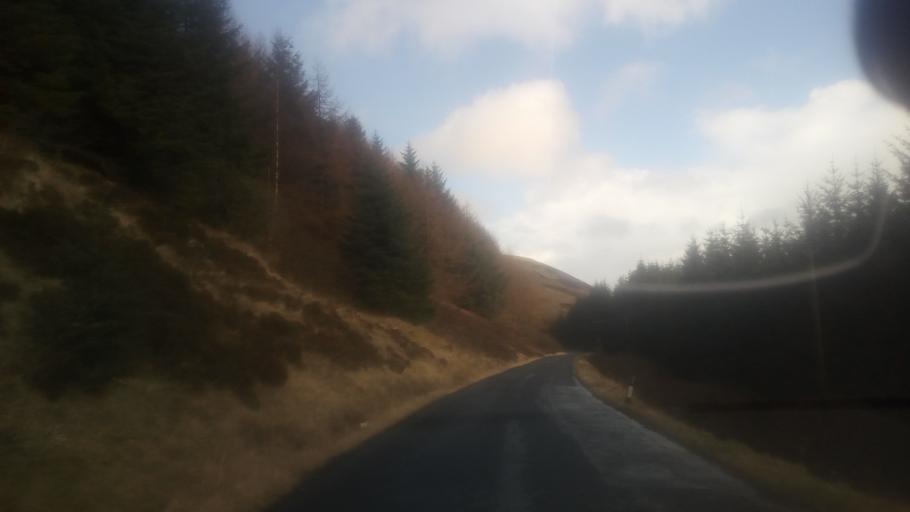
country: GB
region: Scotland
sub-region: The Scottish Borders
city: Innerleithen
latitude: 55.4664
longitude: -3.1350
